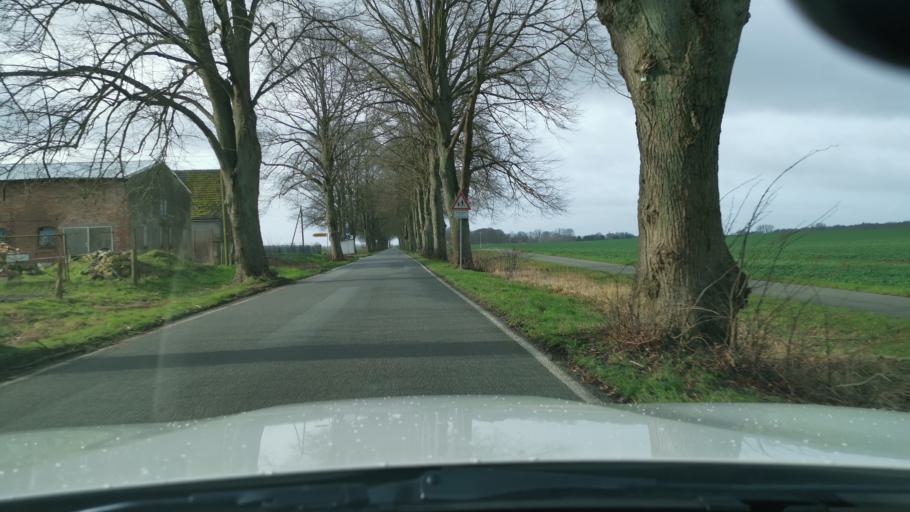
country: DE
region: Mecklenburg-Vorpommern
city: Wardow
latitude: 53.9973
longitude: 12.3796
